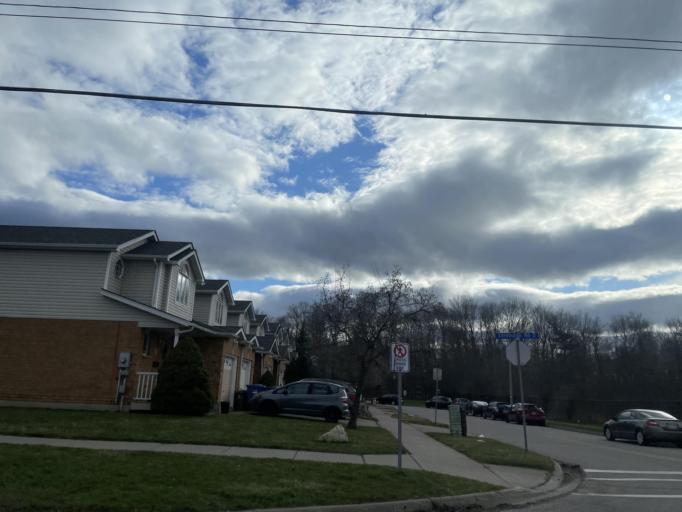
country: CA
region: Ontario
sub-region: Wellington County
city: Guelph
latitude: 43.5122
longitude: -80.2182
